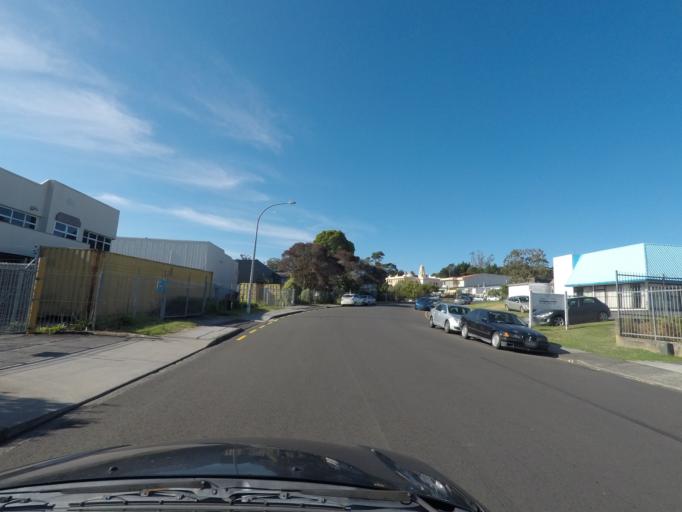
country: NZ
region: Auckland
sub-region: Auckland
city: Rosebank
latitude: -36.9047
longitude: 174.6983
